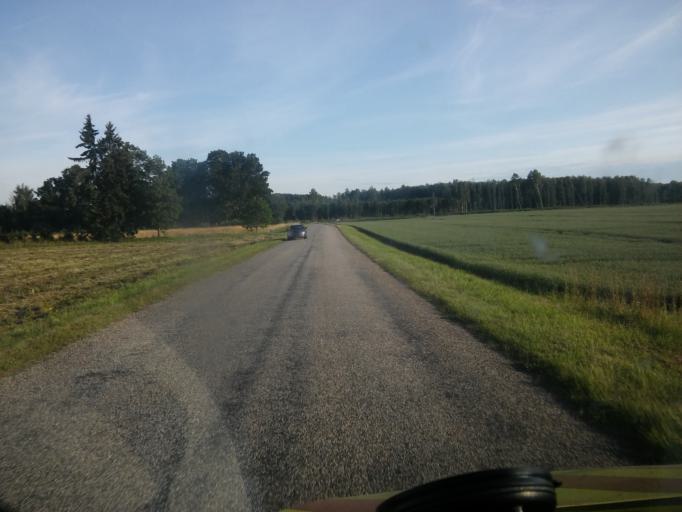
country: EE
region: Valgamaa
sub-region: Torva linn
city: Torva
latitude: 58.0830
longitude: 25.9058
